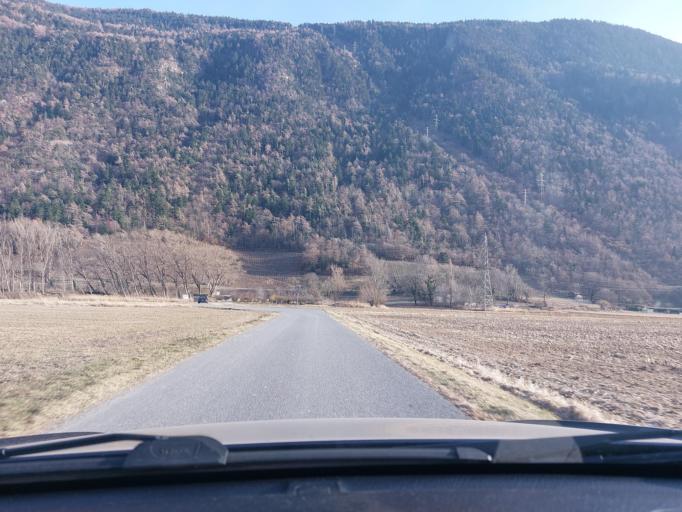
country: CH
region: Valais
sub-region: Martigny District
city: Charrat-les-Chenes
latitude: 46.1086
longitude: 7.1071
